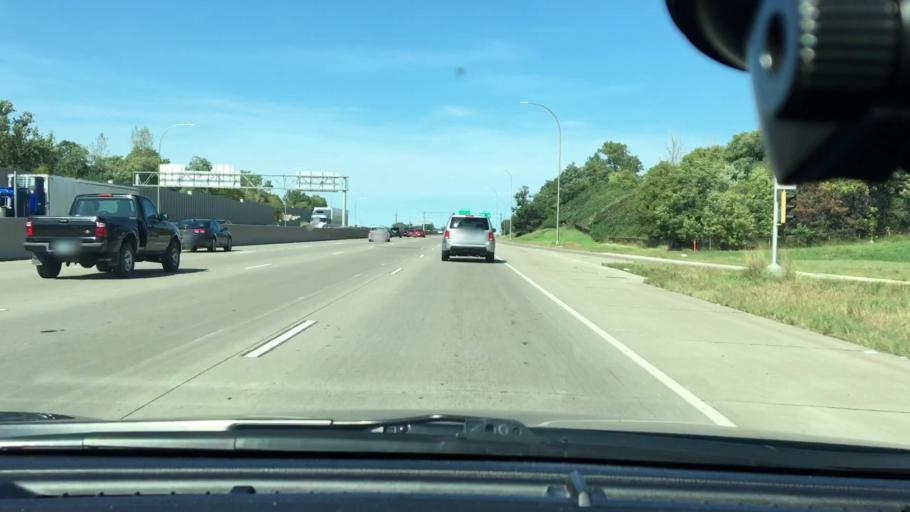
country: US
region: Minnesota
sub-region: Ramsey County
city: Little Canada
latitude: 44.9938
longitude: -93.0892
